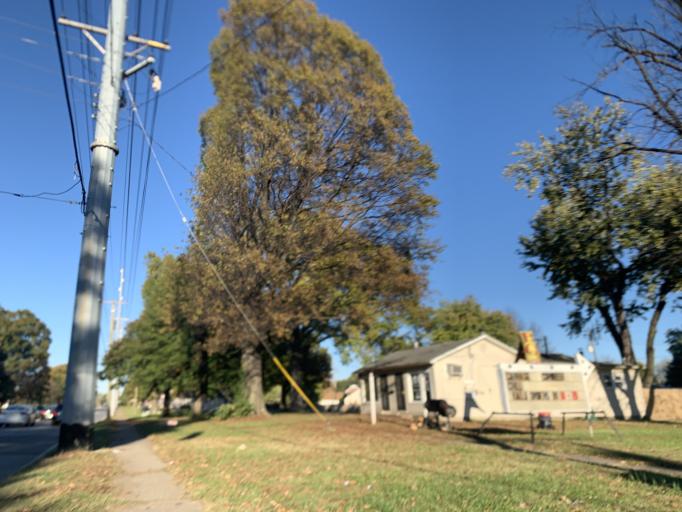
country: US
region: Kentucky
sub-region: Jefferson County
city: Shively
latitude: 38.2149
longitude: -85.7829
